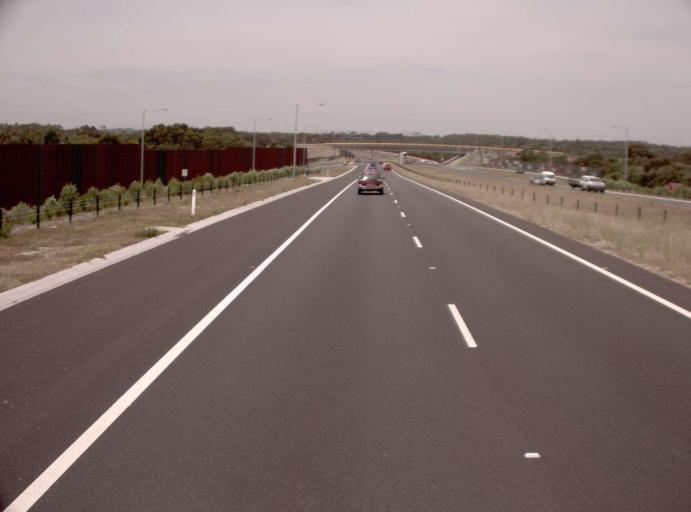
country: AU
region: Victoria
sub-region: Frankston
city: Carrum Downs
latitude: -38.1099
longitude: 145.1625
